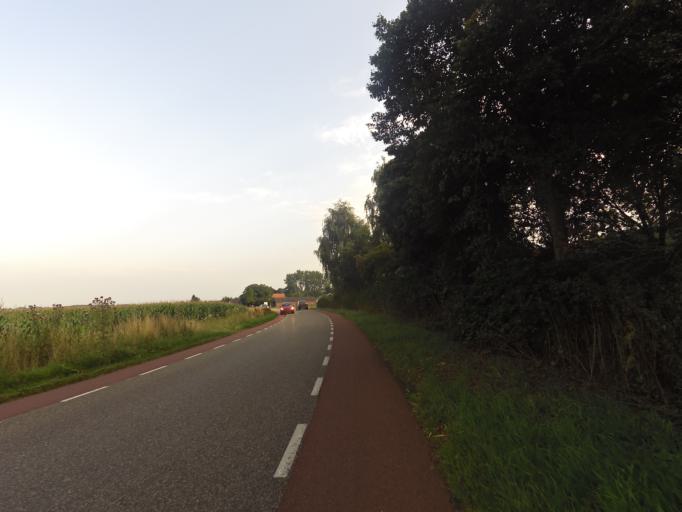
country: NL
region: Gelderland
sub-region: Oude IJsselstreek
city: Gendringen
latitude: 51.8643
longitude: 6.3843
